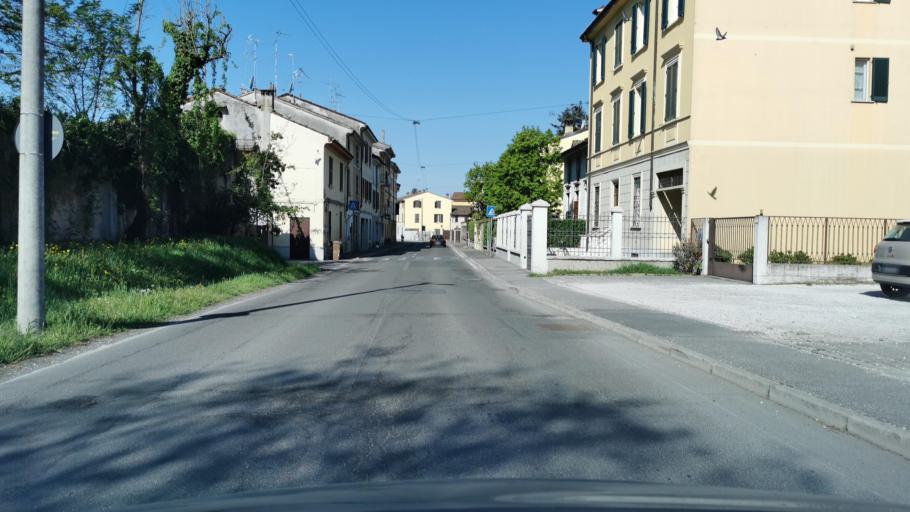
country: IT
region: Lombardy
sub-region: Provincia di Cremona
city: Cremona
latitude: 45.1352
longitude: 10.0439
